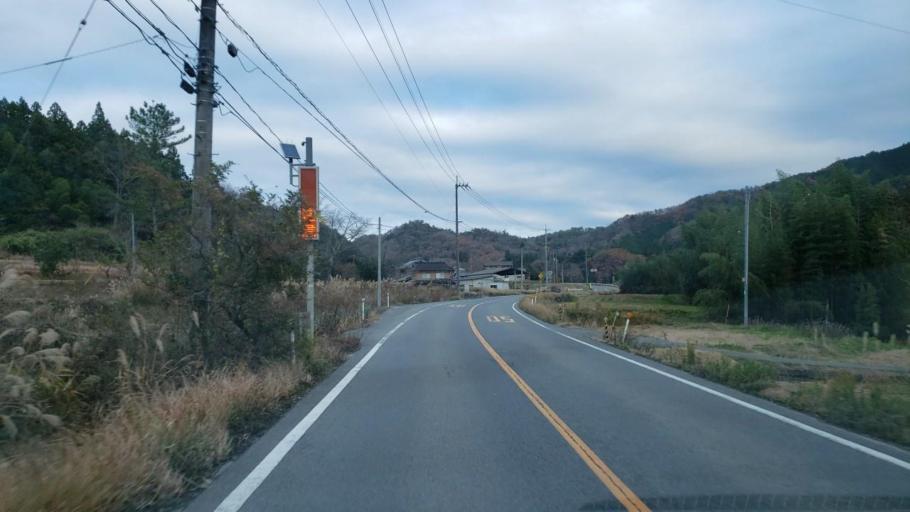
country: JP
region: Tokushima
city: Wakimachi
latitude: 34.1702
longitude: 134.1599
